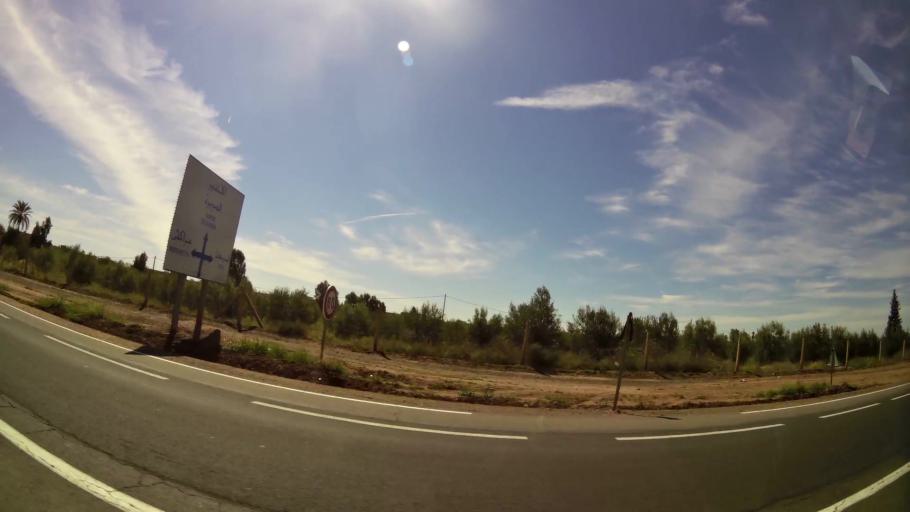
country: MA
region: Marrakech-Tensift-Al Haouz
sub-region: Marrakech
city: Marrakesh
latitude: 31.6429
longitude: -8.1053
